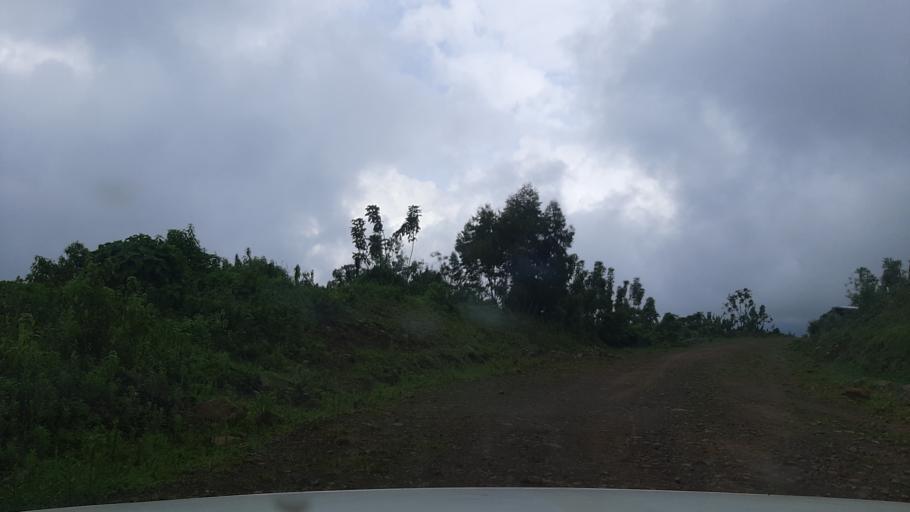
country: ET
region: Southern Nations, Nationalities, and People's Region
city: Bonga
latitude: 7.1155
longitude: 36.5456
